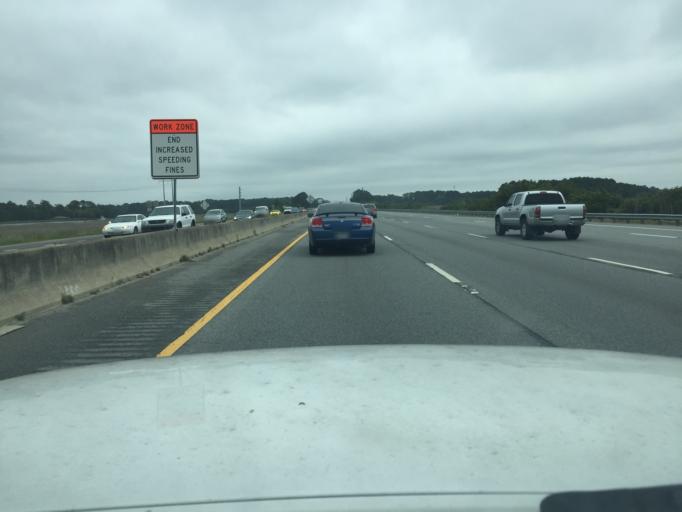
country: US
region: Georgia
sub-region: Chatham County
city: Georgetown
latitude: 31.9842
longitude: -81.1940
